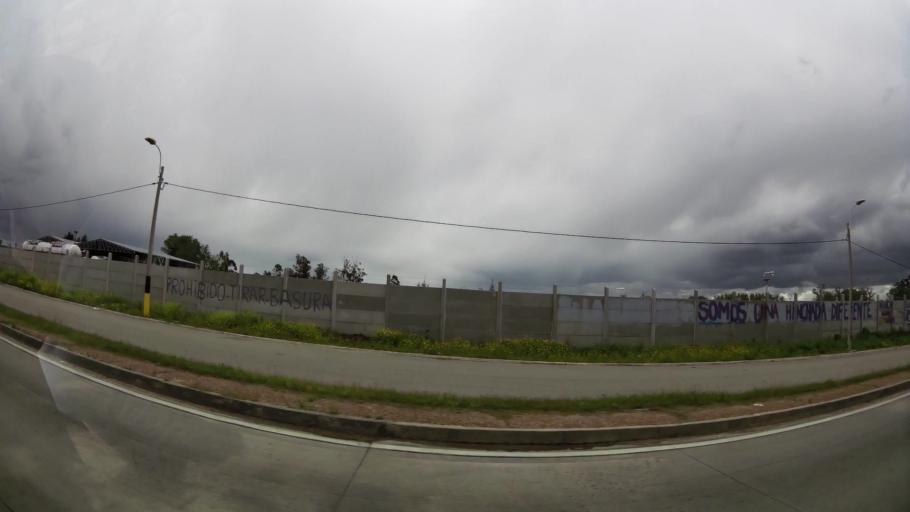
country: UY
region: Canelones
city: Toledo
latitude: -34.7967
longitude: -56.1490
